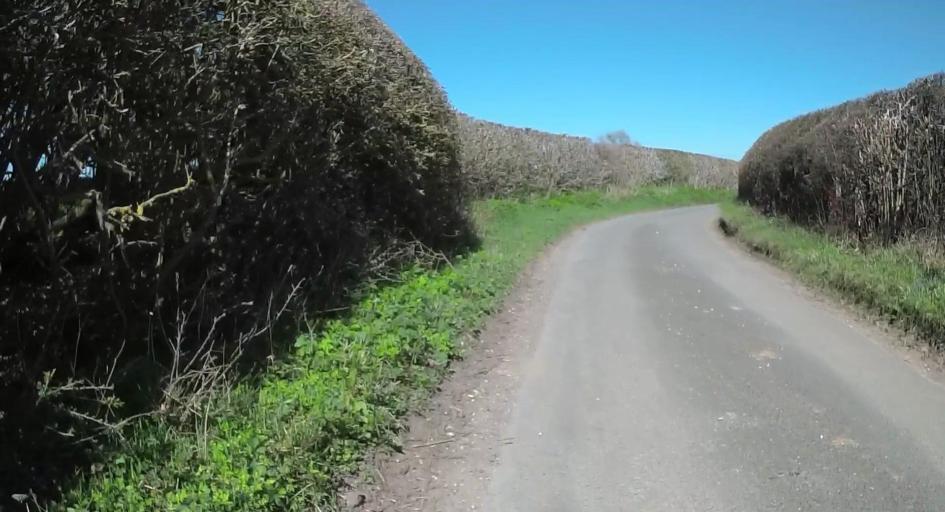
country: GB
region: England
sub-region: Hampshire
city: Kingsclere
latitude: 51.2846
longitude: -1.1768
